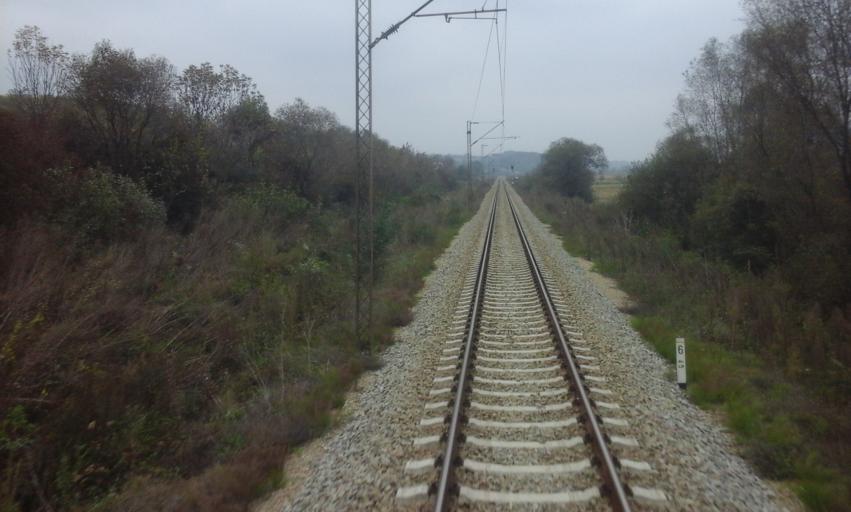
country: RS
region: Central Serbia
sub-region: Belgrade
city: Sopot
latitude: 44.4976
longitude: 20.6472
